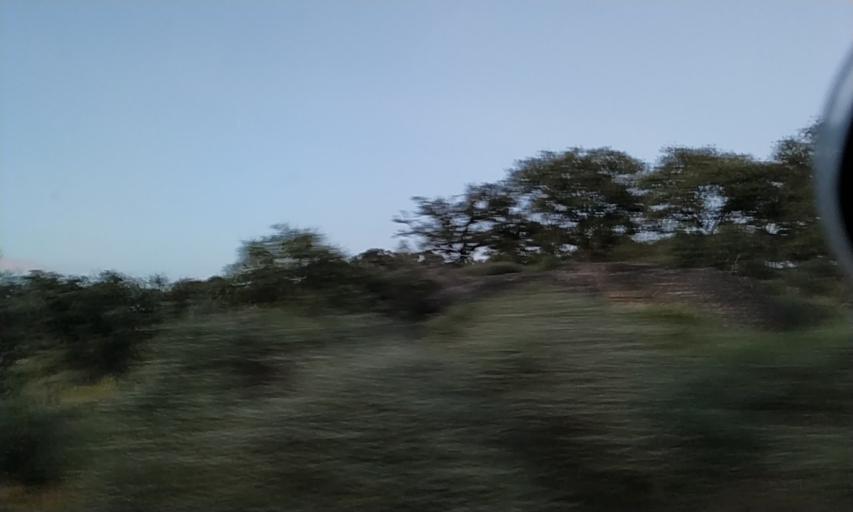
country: ES
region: Extremadura
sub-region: Provincia de Caceres
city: Piedras Albas
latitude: 39.7583
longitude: -6.9049
